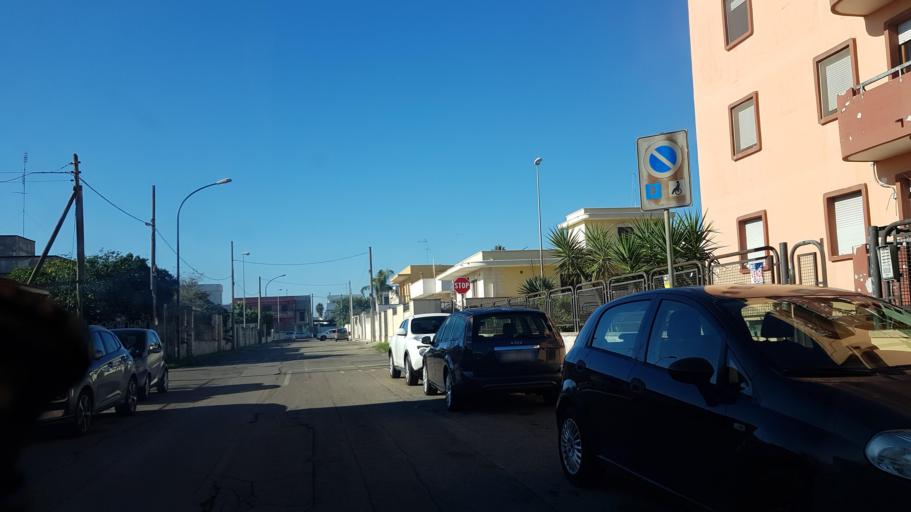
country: IT
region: Apulia
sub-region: Provincia di Lecce
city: Squinzano
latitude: 40.4275
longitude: 18.0428
